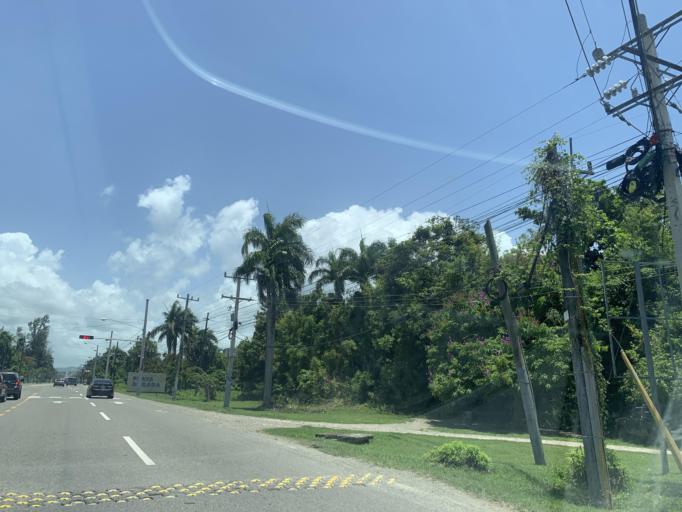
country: DO
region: Puerto Plata
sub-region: Puerto Plata
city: Puerto Plata
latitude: 19.7676
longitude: -70.6515
